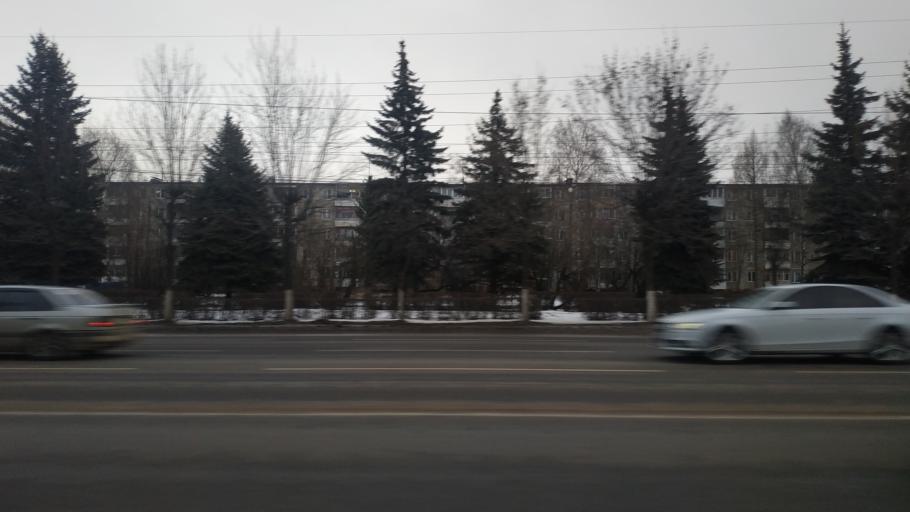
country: RU
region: Tverskaya
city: Tver
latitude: 56.8268
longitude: 35.8954
